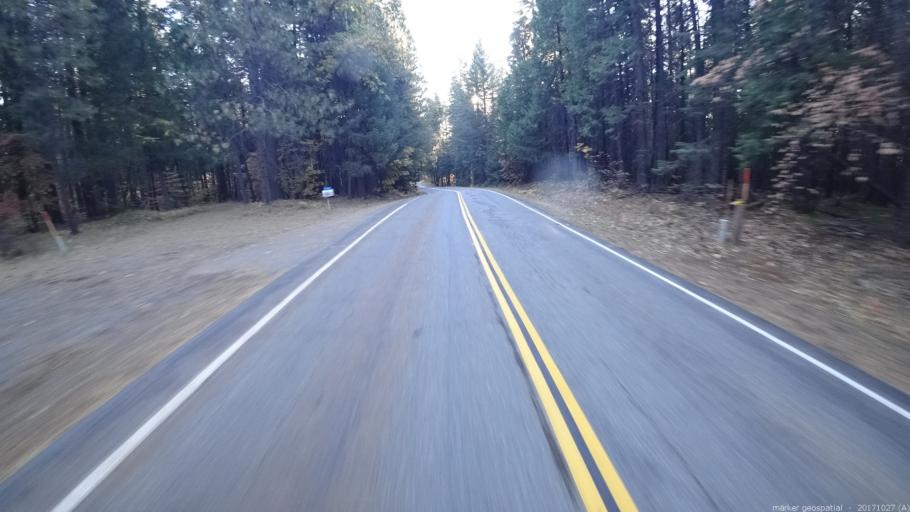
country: US
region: California
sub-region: Shasta County
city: Burney
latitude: 40.9250
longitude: -121.9222
